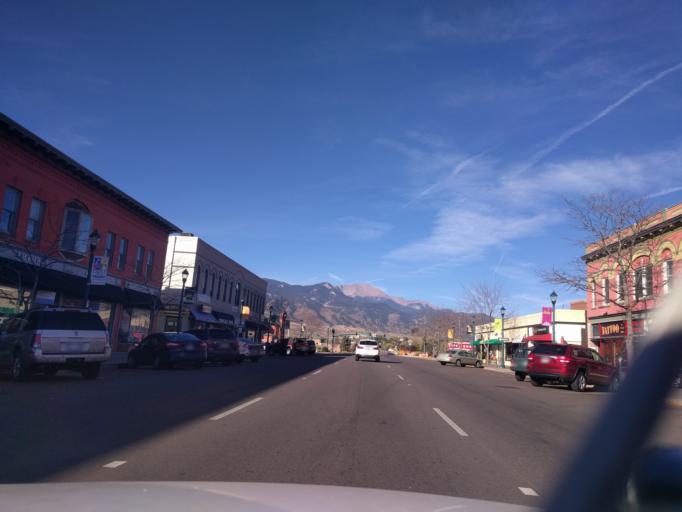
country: US
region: Colorado
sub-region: El Paso County
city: Colorado Springs
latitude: 38.8367
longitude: -104.8238
